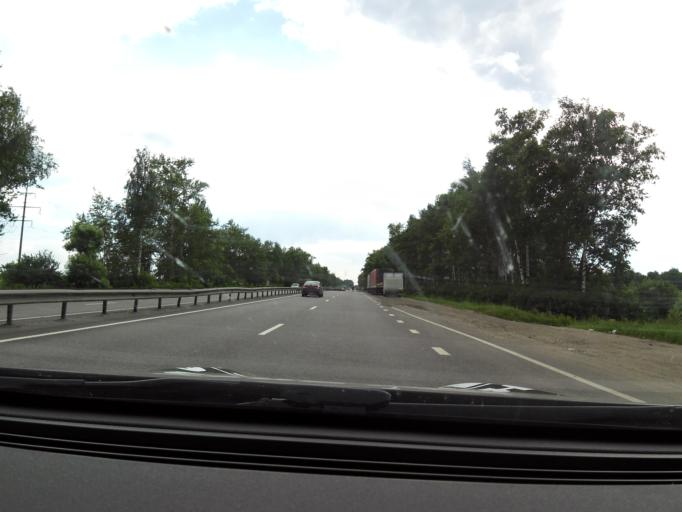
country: RU
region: Vladimir
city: Gorokhovets
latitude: 56.1657
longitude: 42.6205
